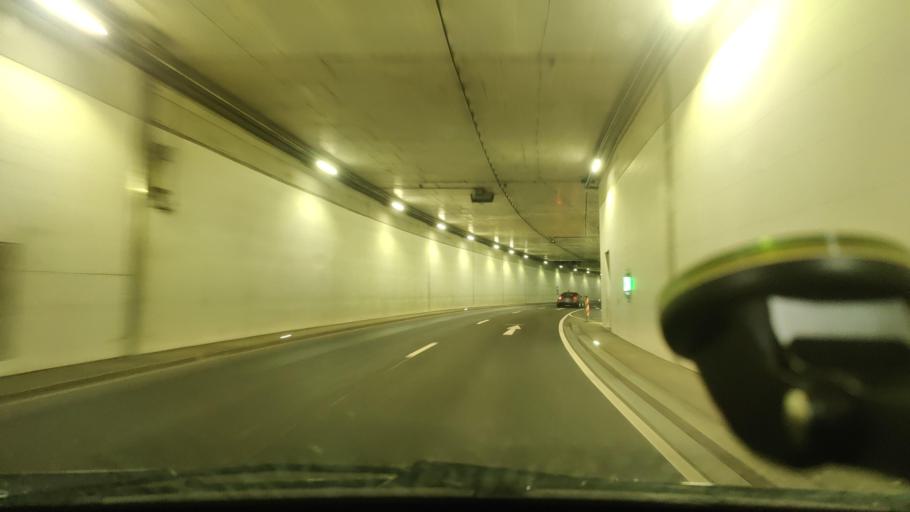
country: DE
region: North Rhine-Westphalia
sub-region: Regierungsbezirk Dusseldorf
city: Dusseldorf
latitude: 51.2272
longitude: 6.7823
